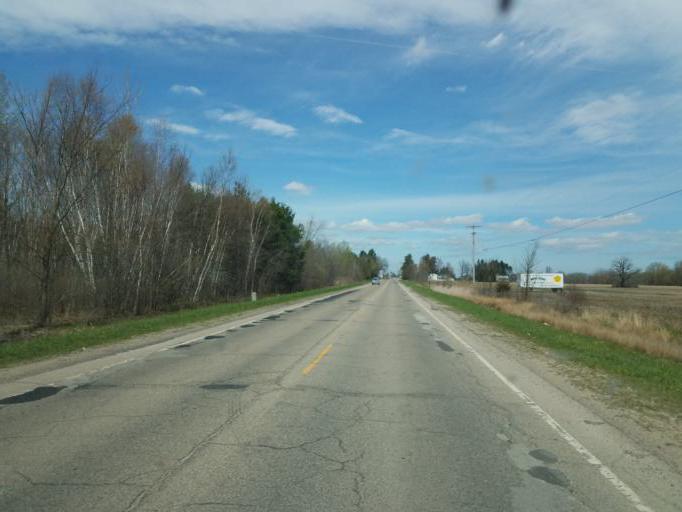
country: US
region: Michigan
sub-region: Isabella County
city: Mount Pleasant
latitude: 43.6343
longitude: -84.7681
